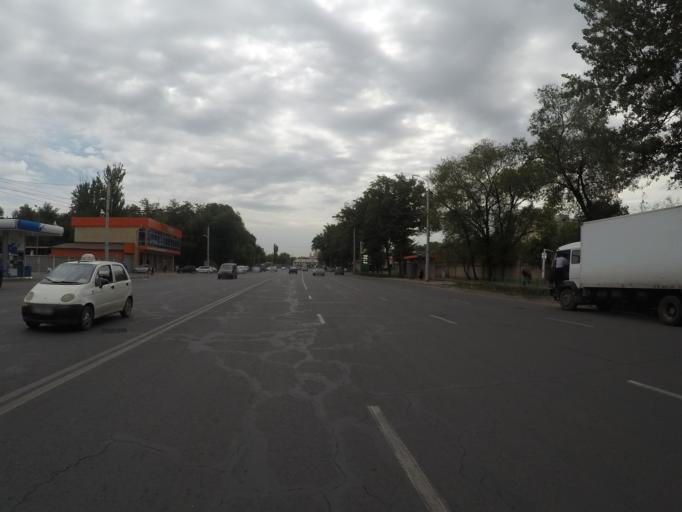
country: KG
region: Chuy
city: Bishkek
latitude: 42.8849
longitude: 74.5724
